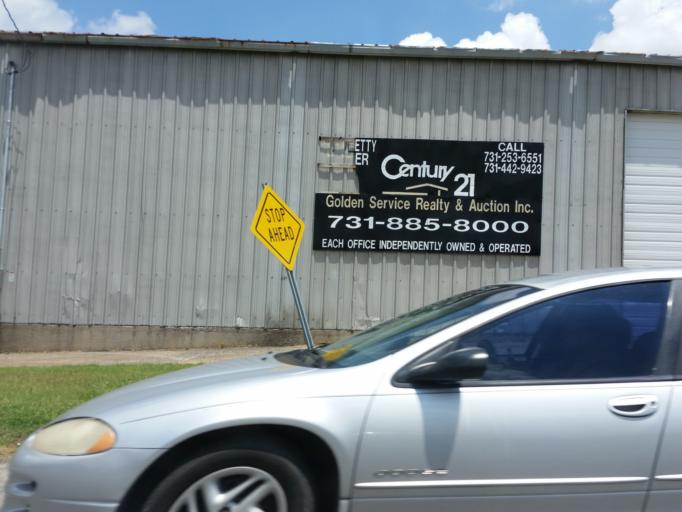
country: US
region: Tennessee
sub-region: Lake County
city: Tiptonville
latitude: 36.3699
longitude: -89.4692
